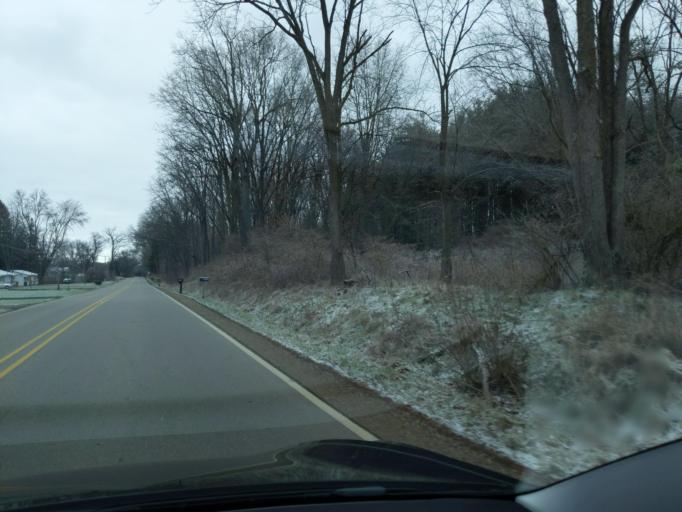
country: US
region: Michigan
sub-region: Jackson County
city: Spring Arbor
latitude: 42.2240
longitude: -84.5167
